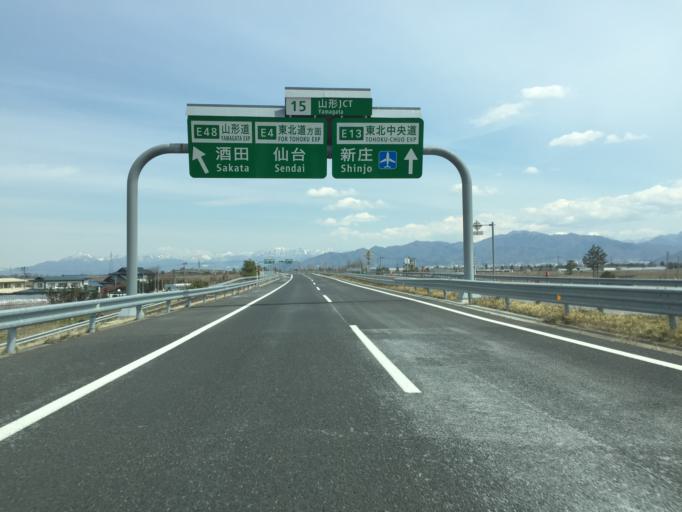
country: JP
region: Yamagata
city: Sagae
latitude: 38.3024
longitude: 140.3089
